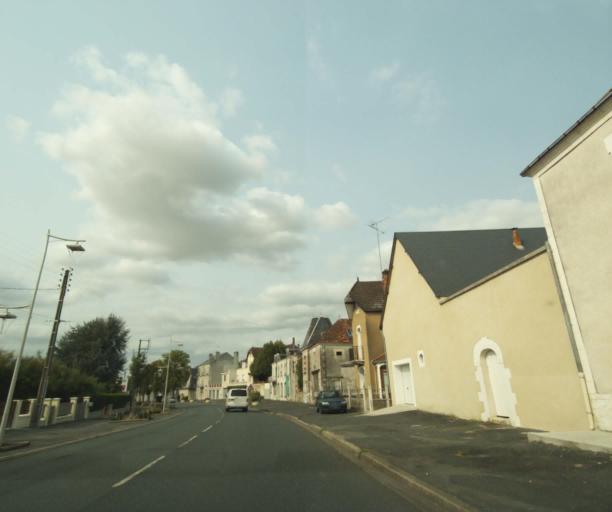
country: FR
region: Centre
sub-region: Departement de l'Indre
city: Chatillon-sur-Indre
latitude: 46.9846
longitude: 1.1733
